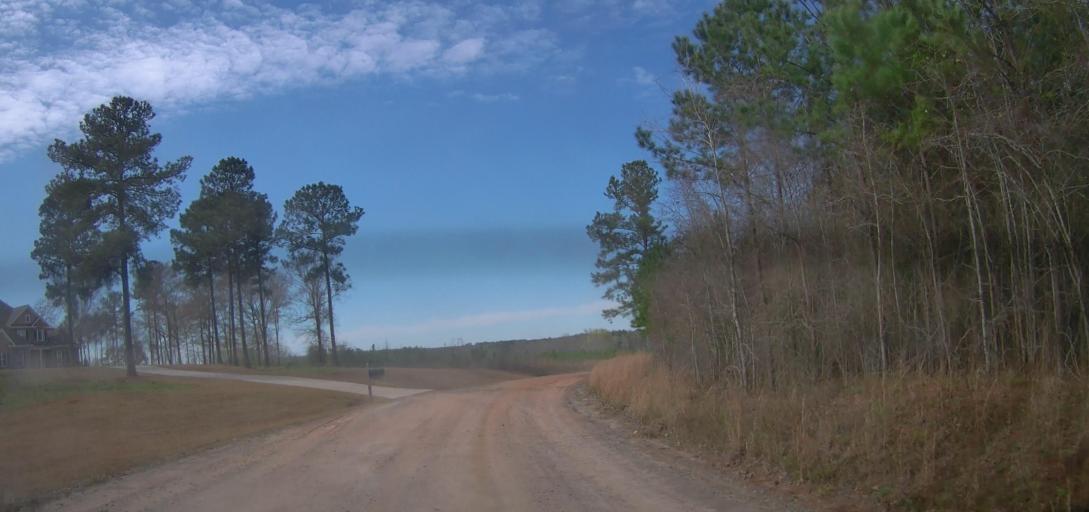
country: US
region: Georgia
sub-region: Monroe County
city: Forsyth
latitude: 33.0322
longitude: -83.8813
